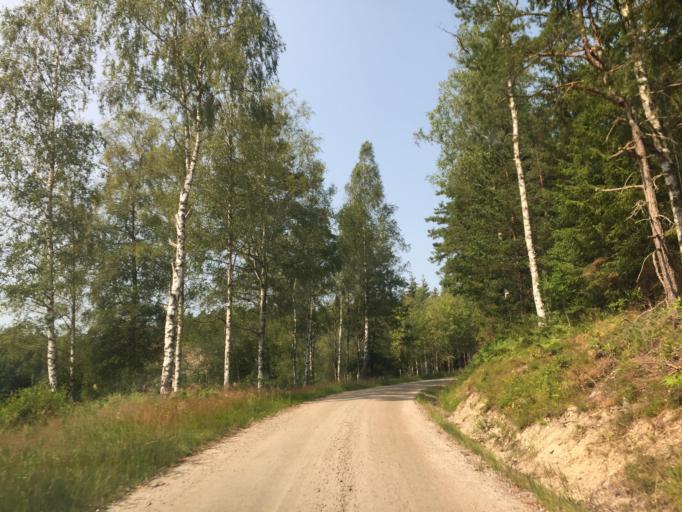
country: SE
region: Vaestra Goetaland
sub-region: Lilla Edets Kommun
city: Lilla Edet
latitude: 58.2433
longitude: 12.0821
